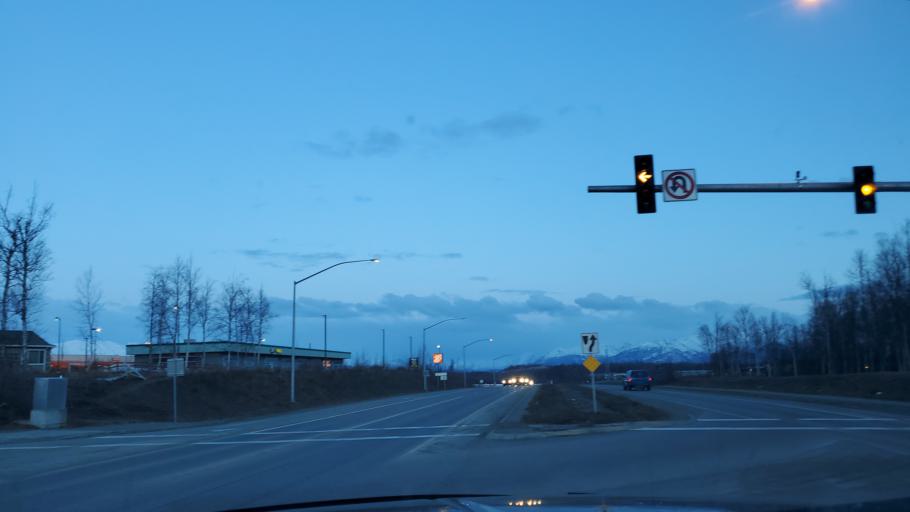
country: US
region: Alaska
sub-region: Matanuska-Susitna Borough
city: Wasilla
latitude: 61.5736
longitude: -149.4205
